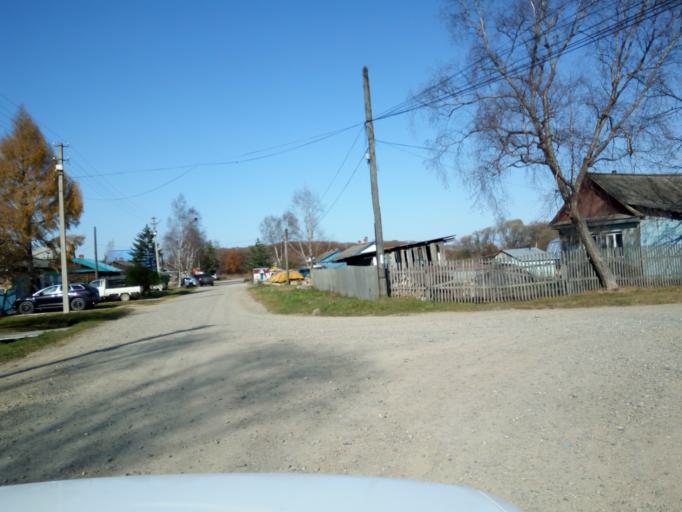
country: RU
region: Primorskiy
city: Dal'nerechensk
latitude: 45.9202
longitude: 133.7119
